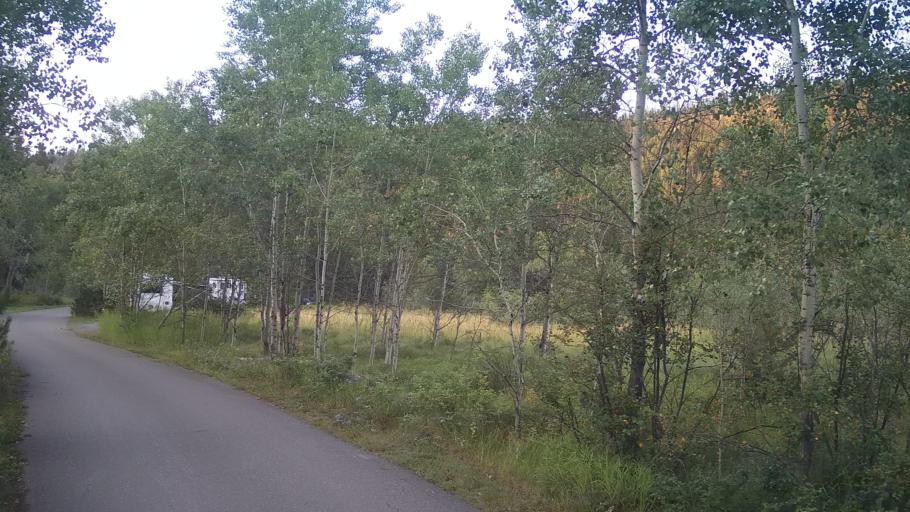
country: CA
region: British Columbia
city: Hanceville
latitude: 52.0889
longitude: -123.3964
